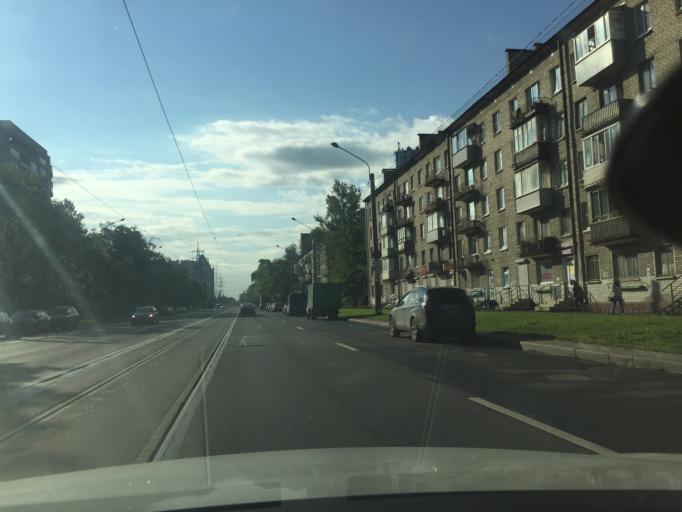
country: RU
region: St.-Petersburg
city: Kupchino
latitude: 59.8376
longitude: 30.3402
